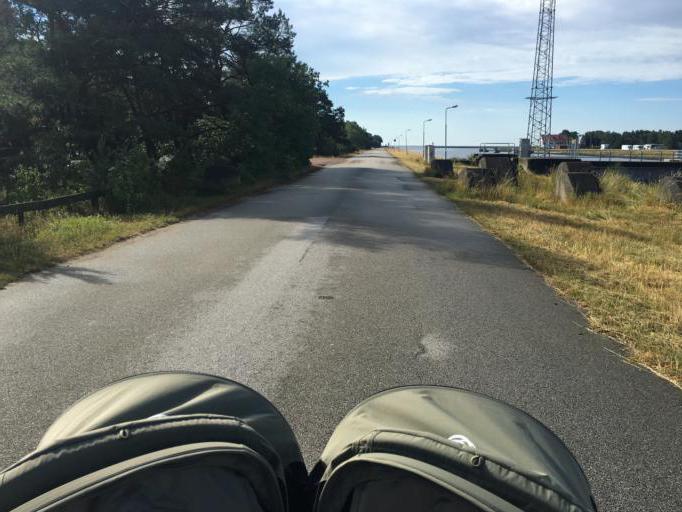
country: SE
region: Skane
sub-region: Vellinge Kommun
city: Hollviken
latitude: 55.4021
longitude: 12.9424
